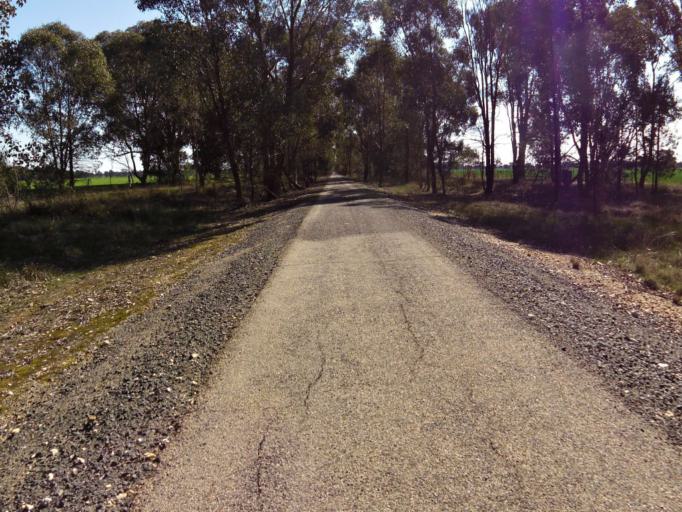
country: AU
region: New South Wales
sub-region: Corowa Shire
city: Corowa
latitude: -36.0261
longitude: 146.4325
